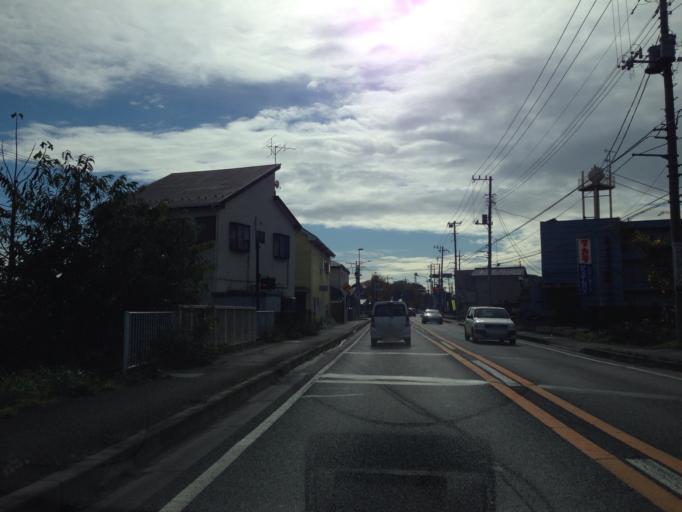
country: JP
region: Ibaraki
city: Naka
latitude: 36.0262
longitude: 140.1610
